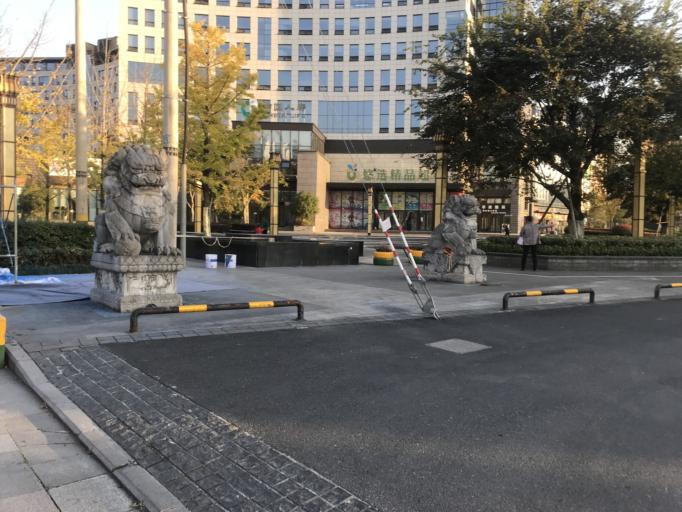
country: CN
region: Anhui Sheng
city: Liyang
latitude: 29.7102
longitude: 118.2854
